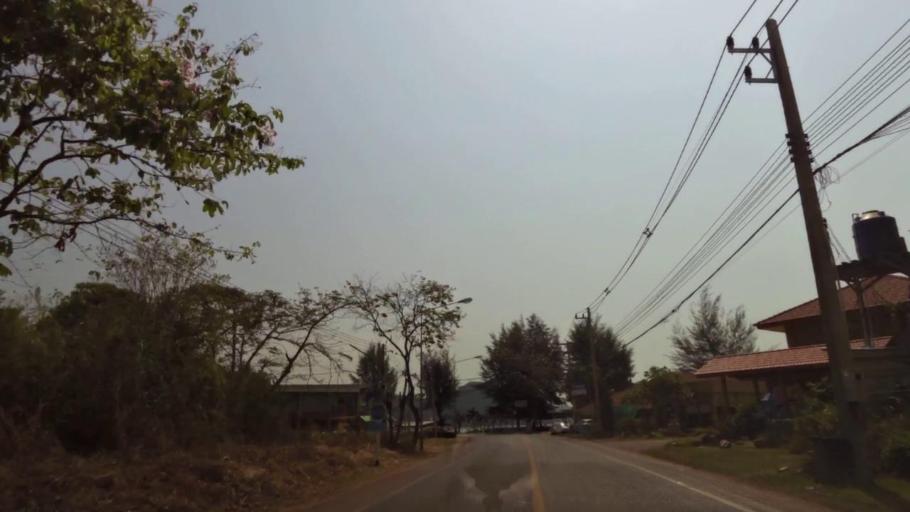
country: TH
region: Chanthaburi
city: Tha Mai
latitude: 12.5338
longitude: 101.9421
